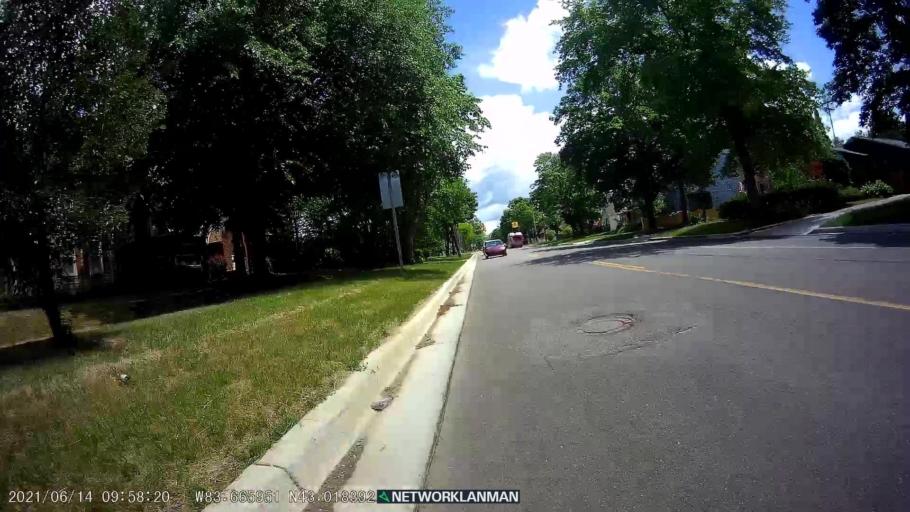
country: US
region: Michigan
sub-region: Genesee County
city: Flint
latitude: 43.0184
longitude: -83.6661
